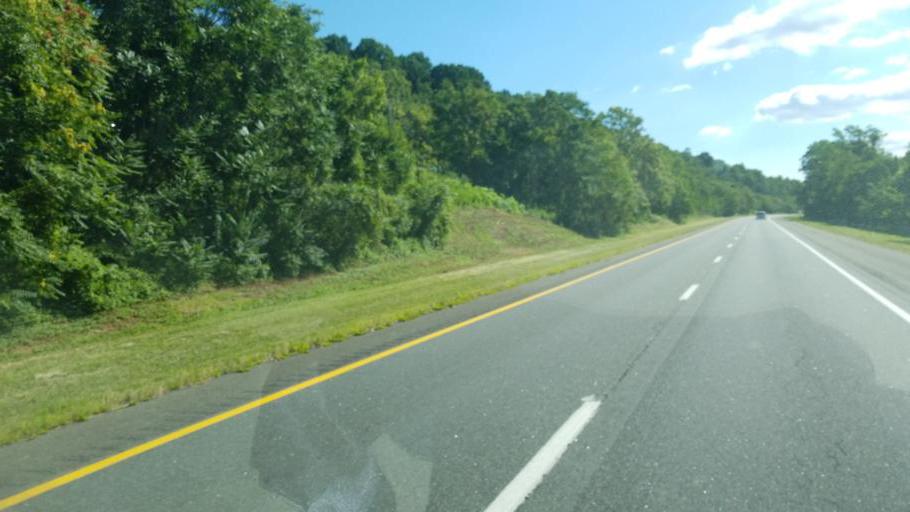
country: US
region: Virginia
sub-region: Warren County
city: Shenandoah Farms
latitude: 38.9084
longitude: -77.9839
